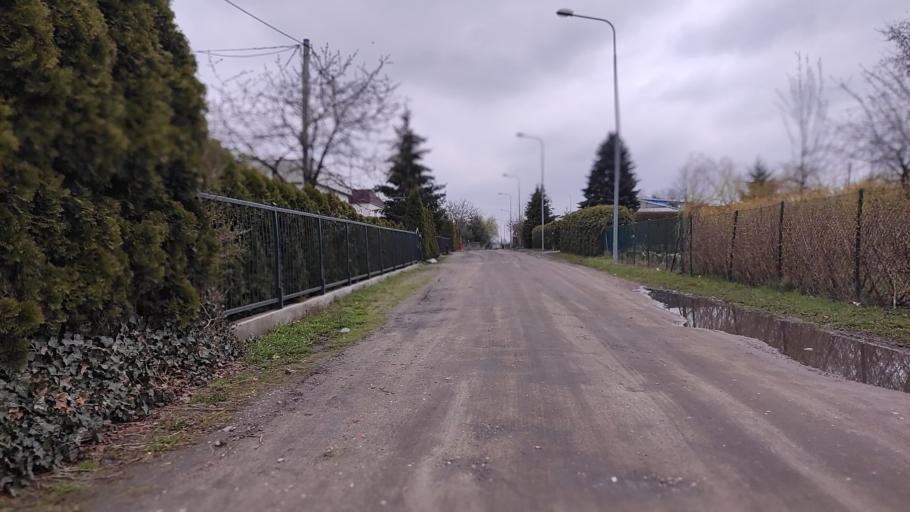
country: PL
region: Greater Poland Voivodeship
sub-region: Powiat poznanski
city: Kleszczewo
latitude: 52.3990
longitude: 17.1604
